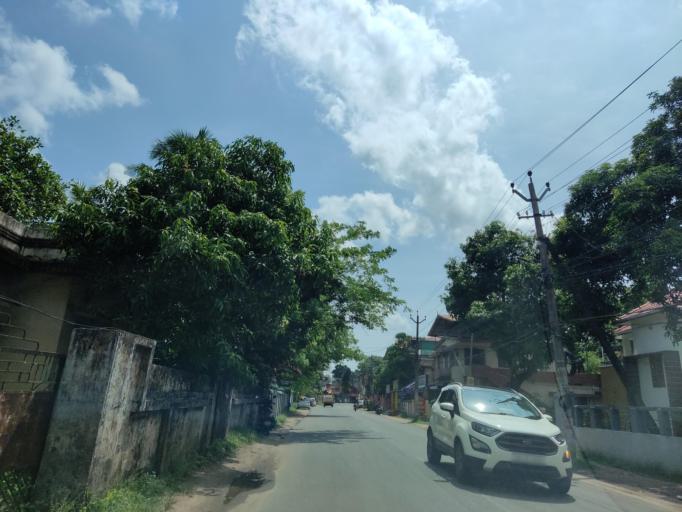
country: IN
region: Kerala
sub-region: Alappuzha
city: Mavelikara
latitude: 9.2564
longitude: 76.5546
